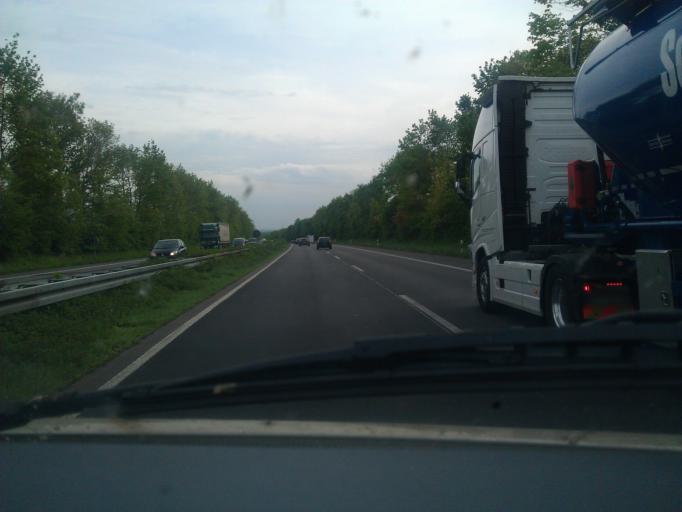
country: DE
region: North Rhine-Westphalia
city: Julich
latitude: 50.9551
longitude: 6.3530
